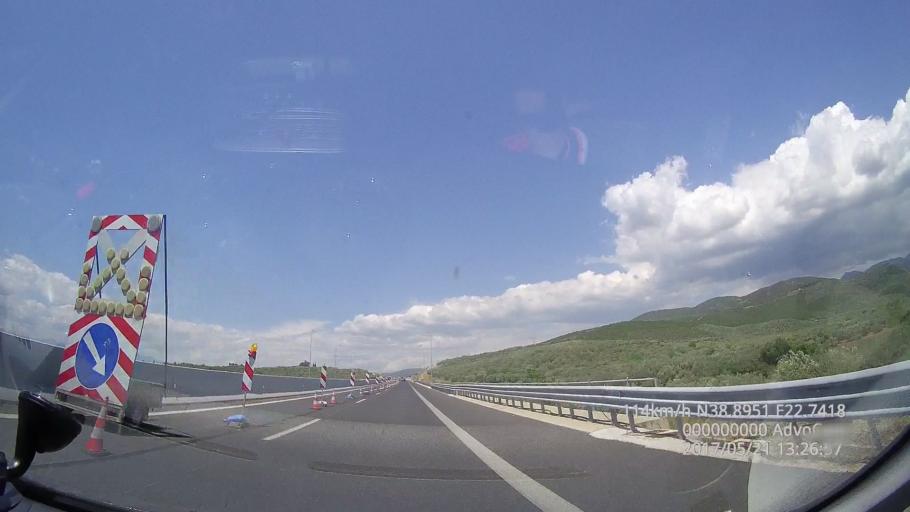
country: GR
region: Central Greece
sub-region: Nomos Fthiotidos
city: Kainouryion
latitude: 38.8953
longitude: 22.7411
